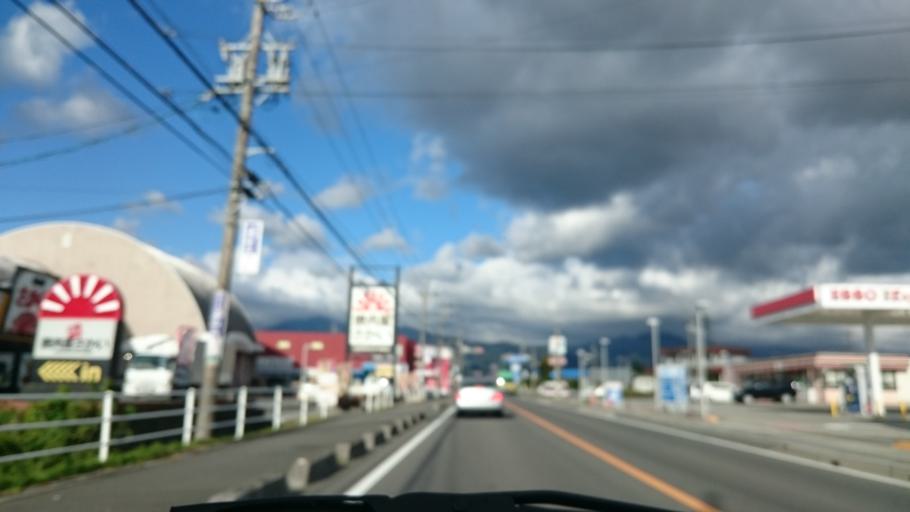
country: JP
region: Mie
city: Komono
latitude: 35.0014
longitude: 136.5356
